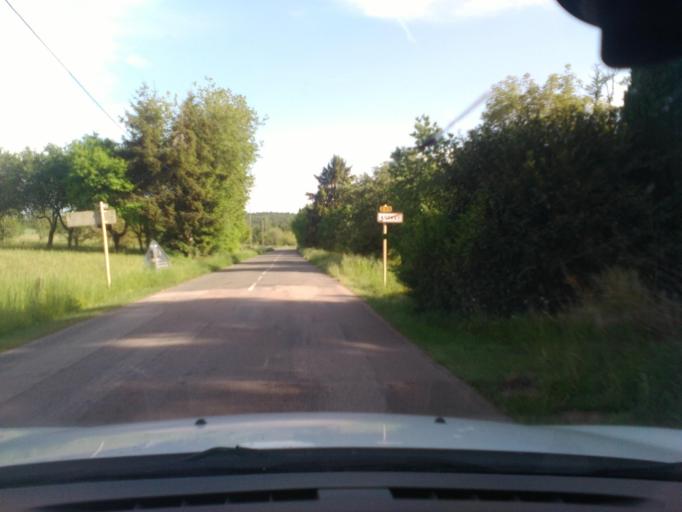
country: FR
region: Lorraine
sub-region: Departement des Vosges
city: Jeanmenil
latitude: 48.2936
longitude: 6.6906
